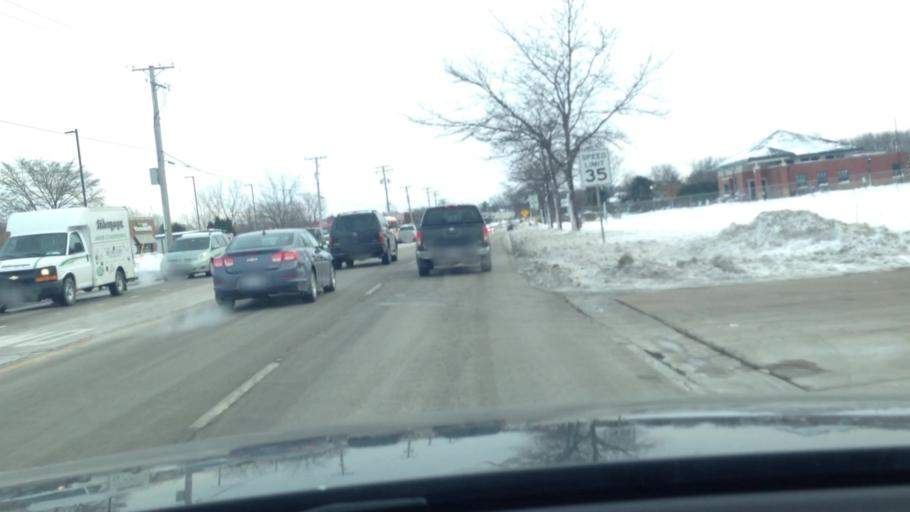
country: US
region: Illinois
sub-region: McHenry County
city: Woodstock
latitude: 42.3126
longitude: -88.4343
